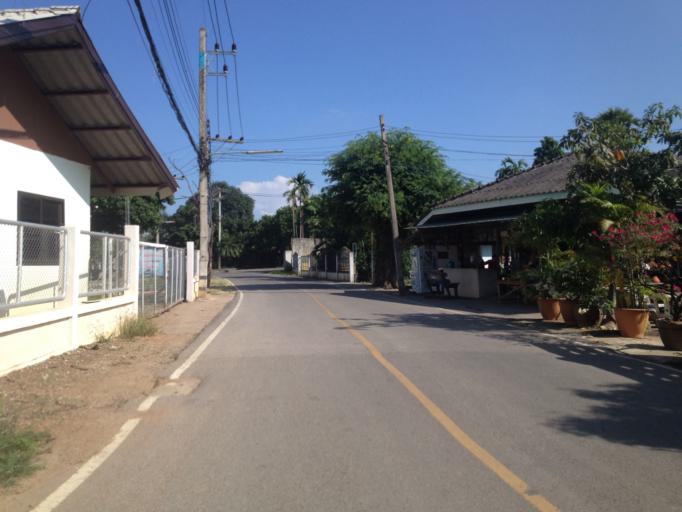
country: TH
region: Chiang Mai
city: Chiang Mai
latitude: 18.7498
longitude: 98.9370
